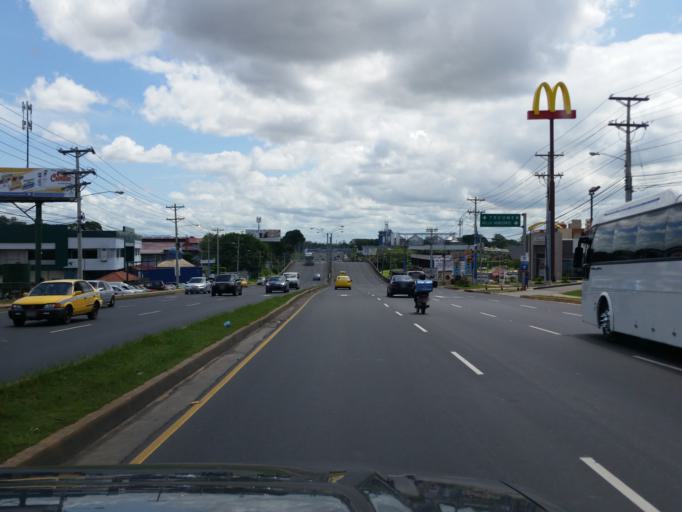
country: PA
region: Panama
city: Tocumen
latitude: 9.0629
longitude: -79.4201
